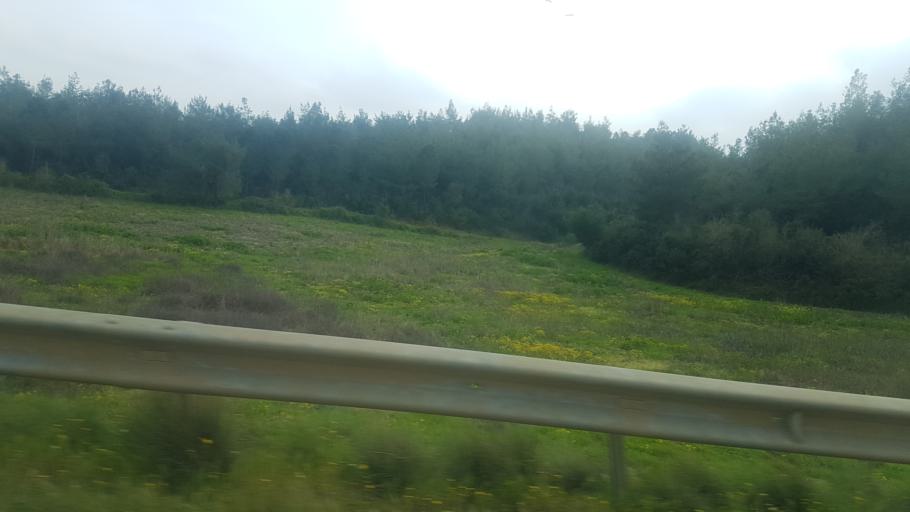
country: TR
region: Mersin
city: Yenice
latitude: 37.0896
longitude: 35.1583
